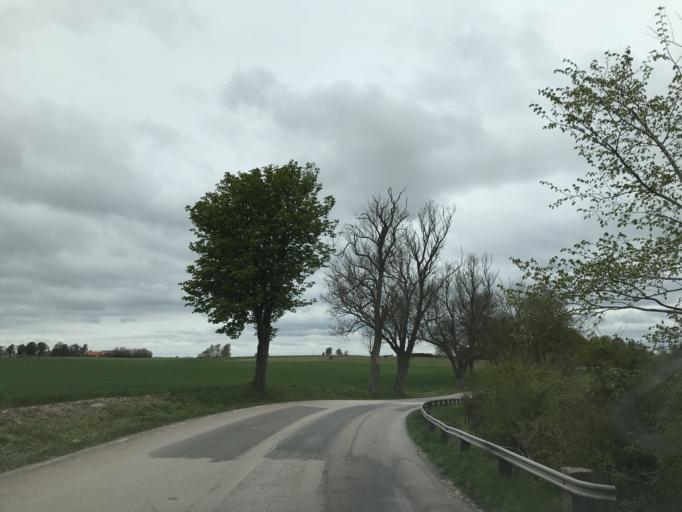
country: SE
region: Skane
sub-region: Eslovs Kommun
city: Eslov
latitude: 55.8715
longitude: 13.2442
